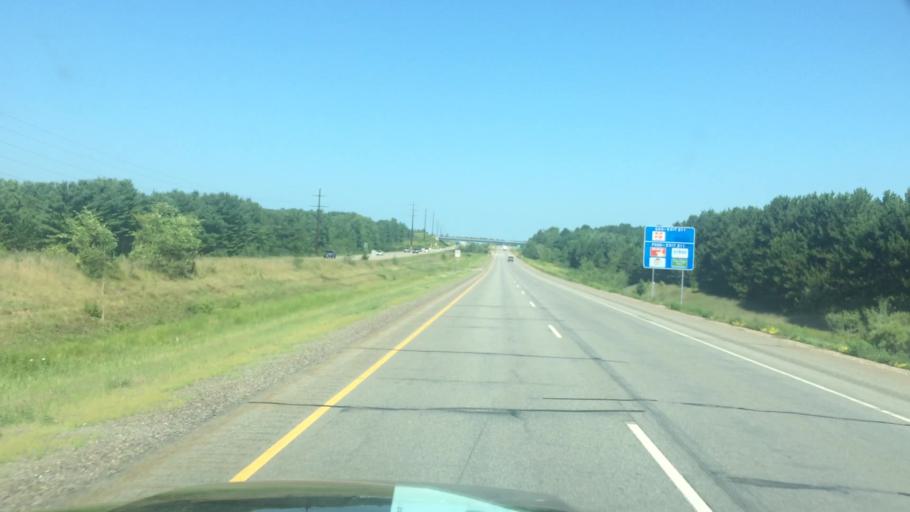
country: US
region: Wisconsin
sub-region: Lincoln County
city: Merrill
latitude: 45.2022
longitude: -89.6556
